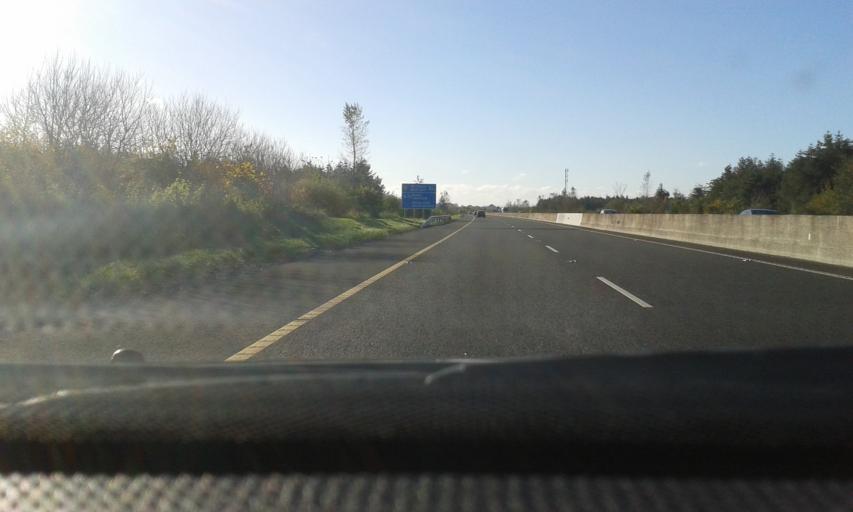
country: IE
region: Munster
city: Thurles
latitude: 52.6817
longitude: -7.6787
